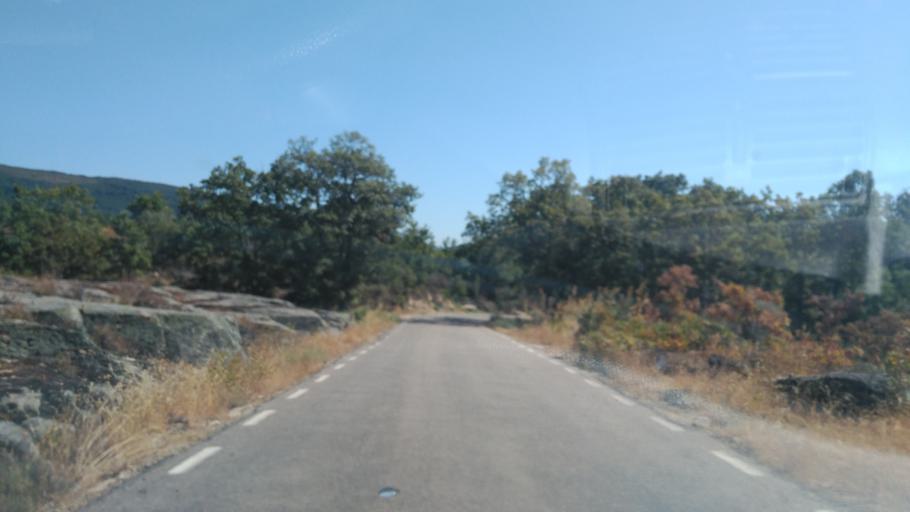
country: ES
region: Castille and Leon
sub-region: Provincia de Salamanca
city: San Martin del Castanar
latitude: 40.5248
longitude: -6.0802
